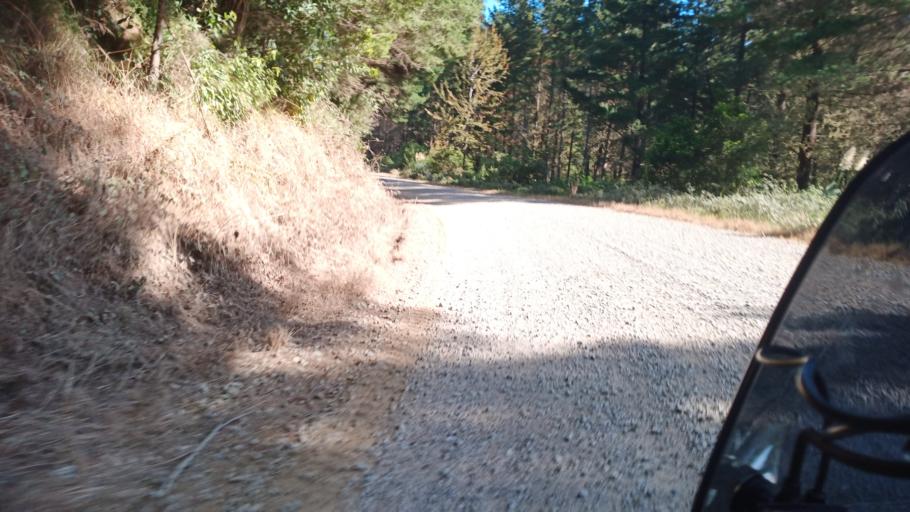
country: NZ
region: Hawke's Bay
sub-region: Wairoa District
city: Wairoa
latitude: -38.9294
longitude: 177.2234
